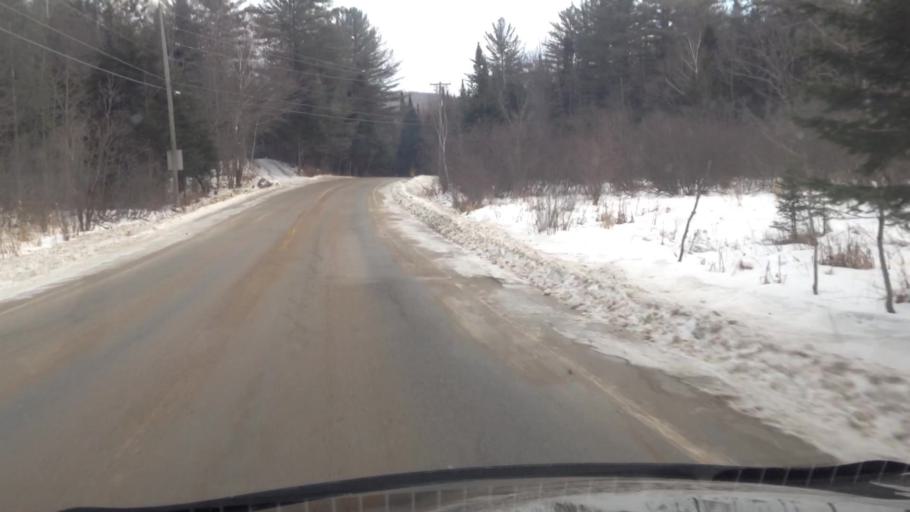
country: CA
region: Quebec
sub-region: Laurentides
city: Brownsburg-Chatham
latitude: 45.9232
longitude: -74.5323
